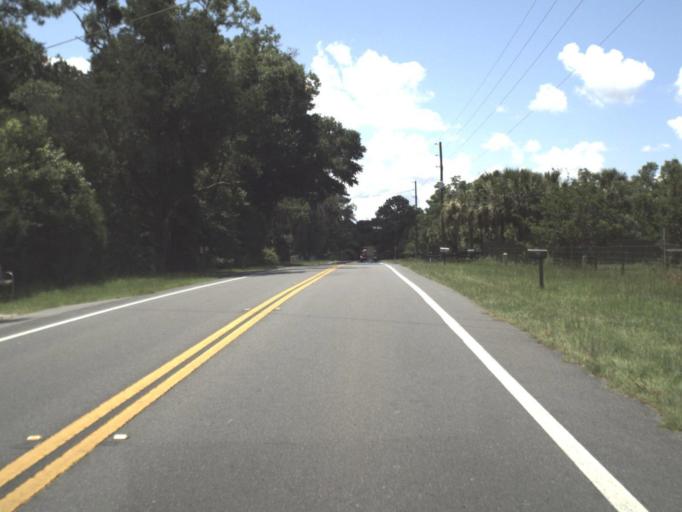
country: US
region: Florida
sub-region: Clay County
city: Keystone Heights
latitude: 29.6865
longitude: -82.0371
